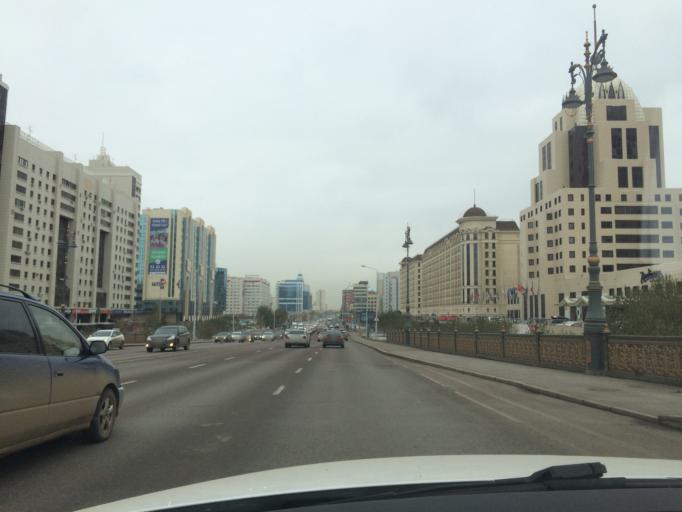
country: KZ
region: Astana Qalasy
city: Astana
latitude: 51.1587
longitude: 71.4112
